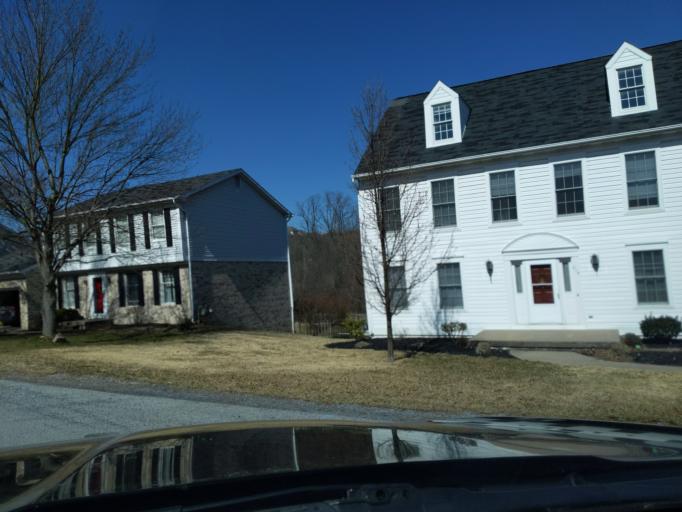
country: US
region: Pennsylvania
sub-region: Blair County
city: Hollidaysburg
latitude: 40.4213
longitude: -78.4081
